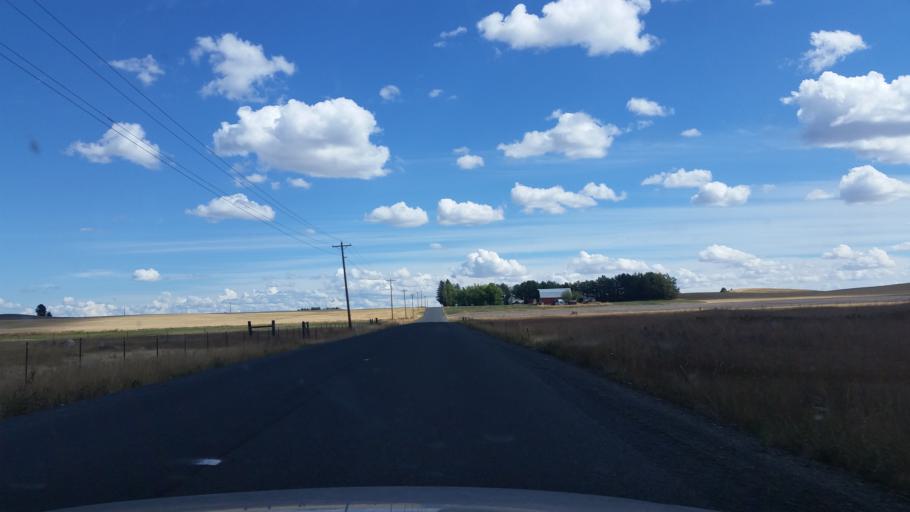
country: US
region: Washington
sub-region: Spokane County
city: Cheney
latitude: 47.5004
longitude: -117.6493
